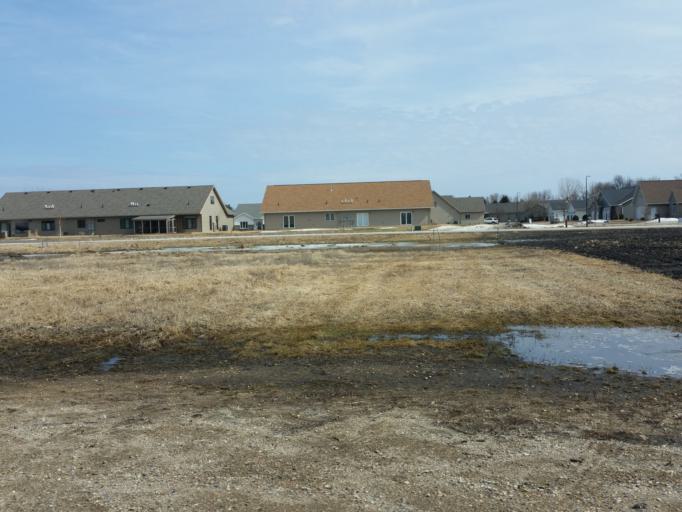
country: US
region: North Dakota
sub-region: Walsh County
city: Grafton
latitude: 48.4060
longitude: -97.4204
